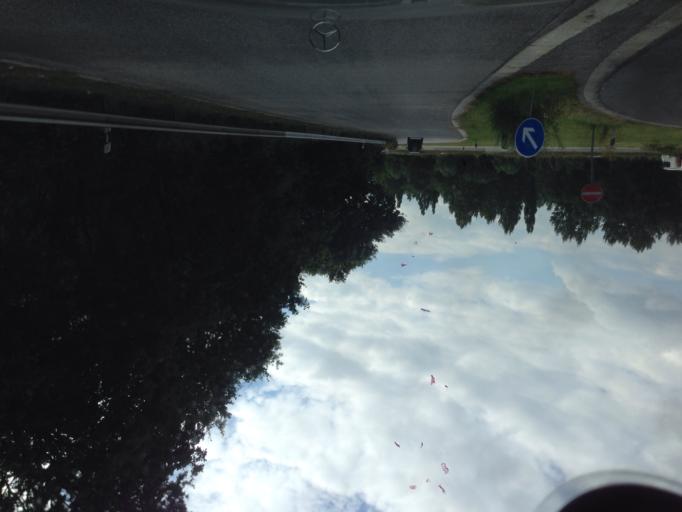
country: DE
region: Schleswig-Holstein
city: Oststeinbek
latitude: 53.5256
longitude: 10.1293
